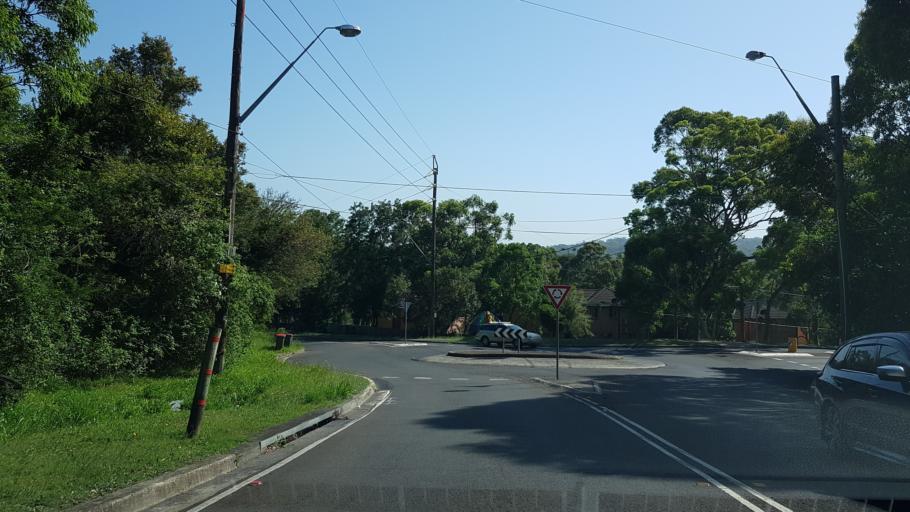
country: AU
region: New South Wales
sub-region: Warringah
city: Narraweena
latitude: -33.7426
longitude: 151.2679
